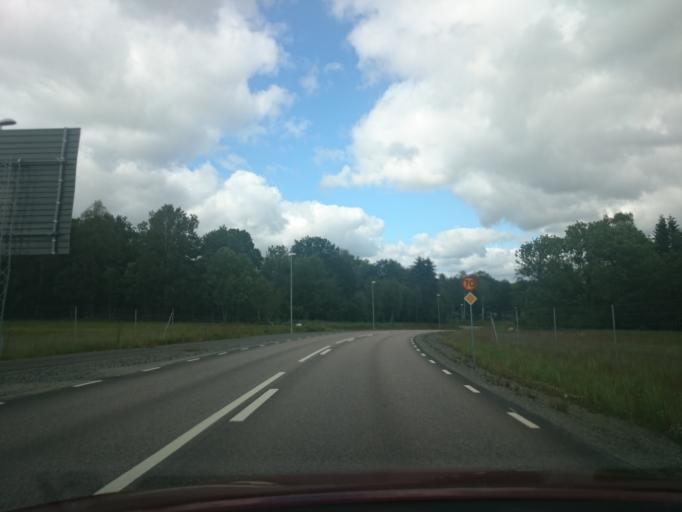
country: SE
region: Vaestra Goetaland
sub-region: Harryda Kommun
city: Landvetter
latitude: 57.6858
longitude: 12.1670
